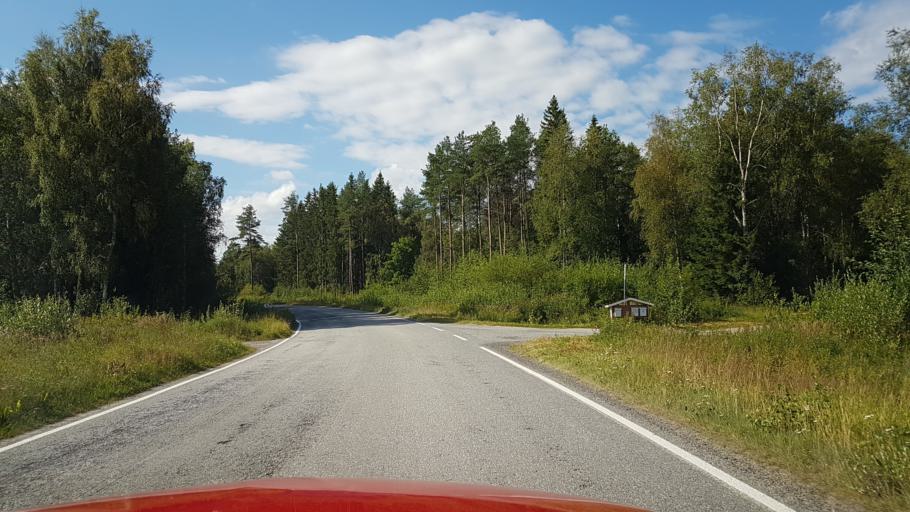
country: FI
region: Northern Ostrobothnia
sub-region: Ylivieska
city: Himanka
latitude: 64.0931
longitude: 23.7656
